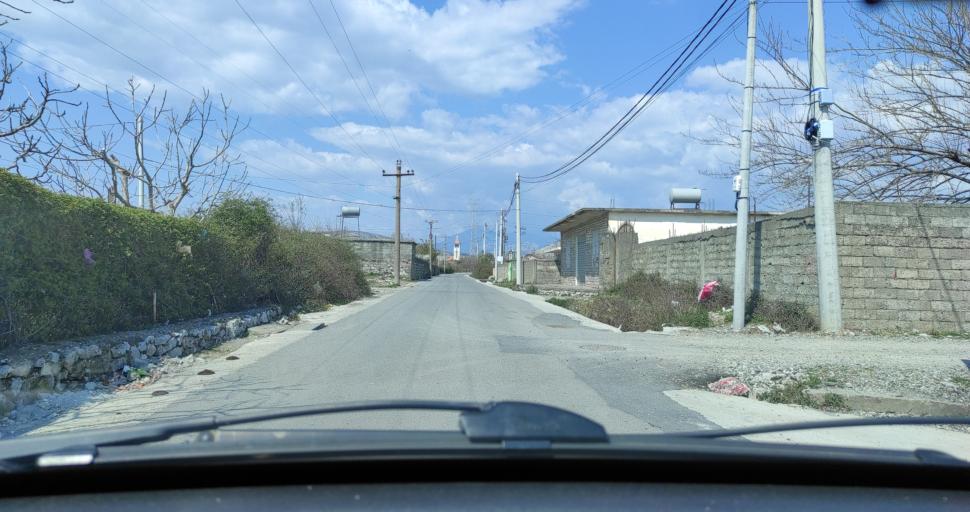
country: AL
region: Shkoder
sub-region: Rrethi i Shkodres
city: Vau i Dejes
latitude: 42.0018
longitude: 19.6423
